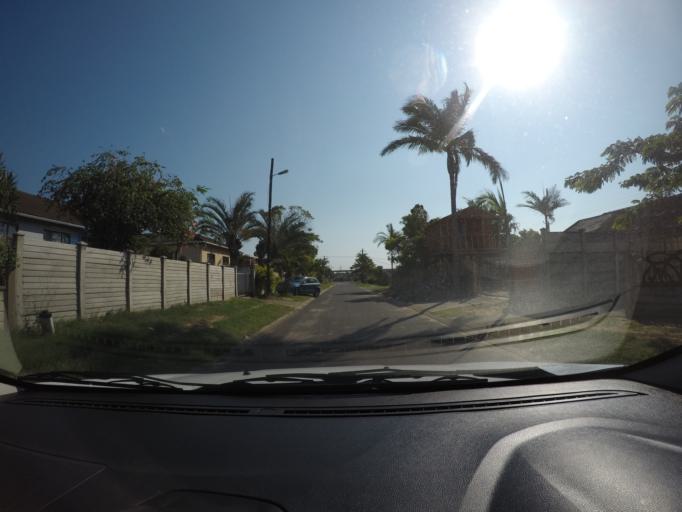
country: ZA
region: KwaZulu-Natal
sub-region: uThungulu District Municipality
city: Richards Bay
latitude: -28.7177
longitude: 32.0404
